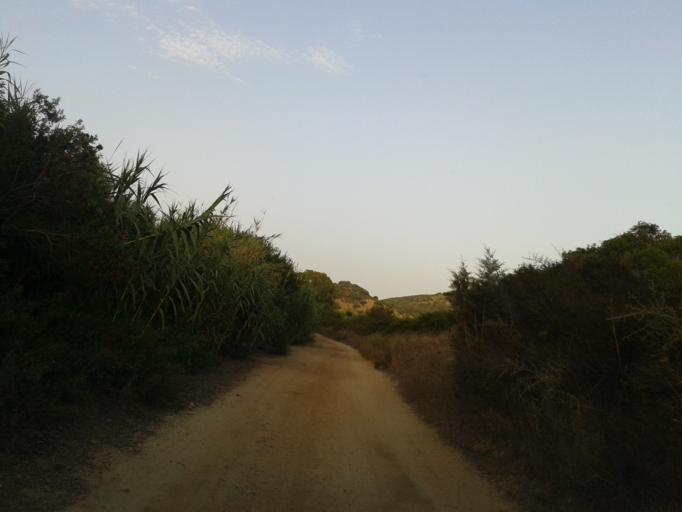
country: IT
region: Sardinia
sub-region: Provincia di Cagliari
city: Villasimius
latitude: 39.1380
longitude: 9.4929
